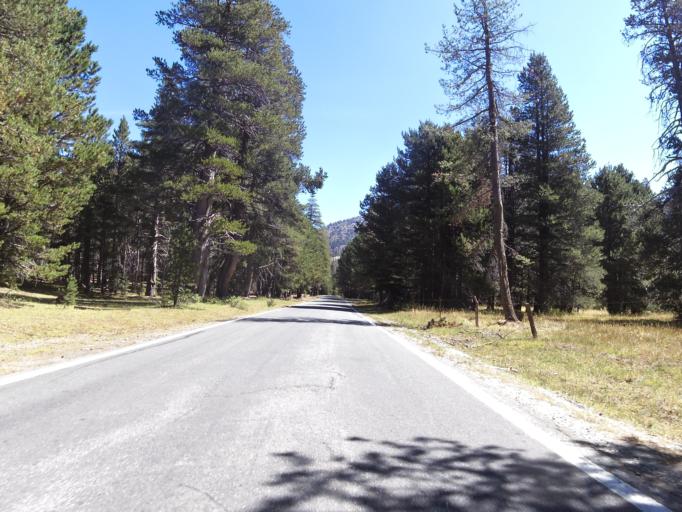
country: US
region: Nevada
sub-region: Douglas County
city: Gardnerville Ranchos
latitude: 38.5384
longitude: -119.8959
